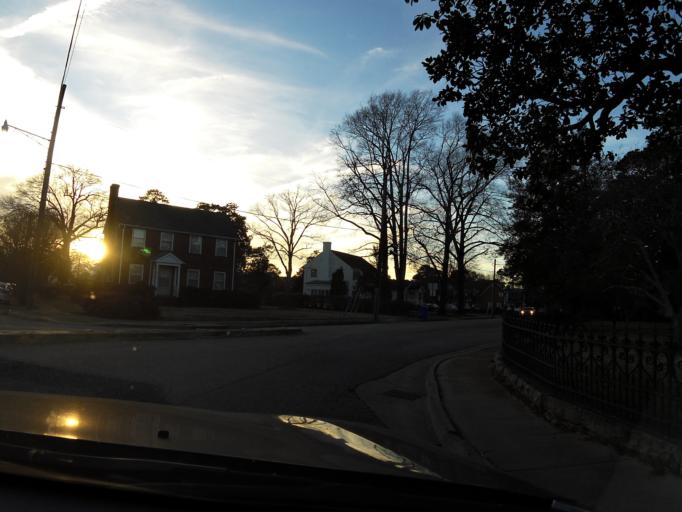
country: US
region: Virginia
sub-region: City of Franklin
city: Franklin
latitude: 36.6775
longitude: -76.9262
